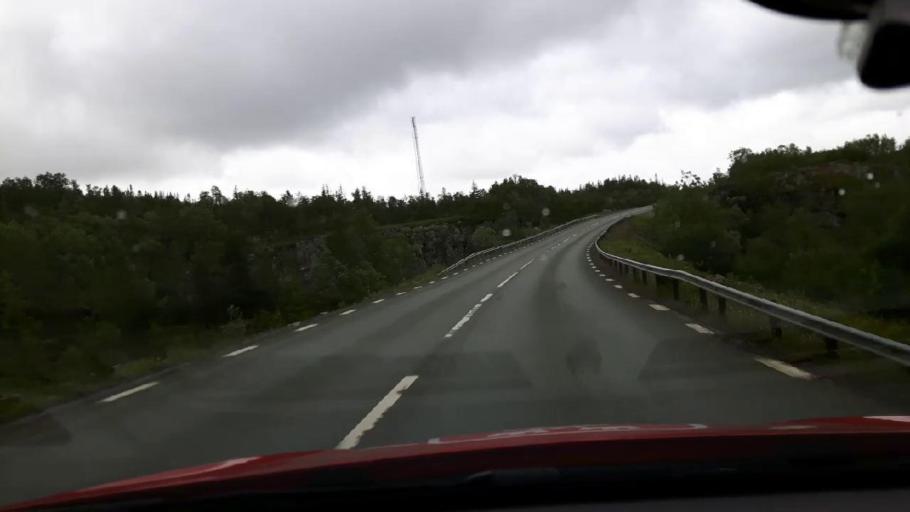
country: NO
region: Nord-Trondelag
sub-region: Meraker
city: Meraker
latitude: 63.3250
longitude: 12.0655
